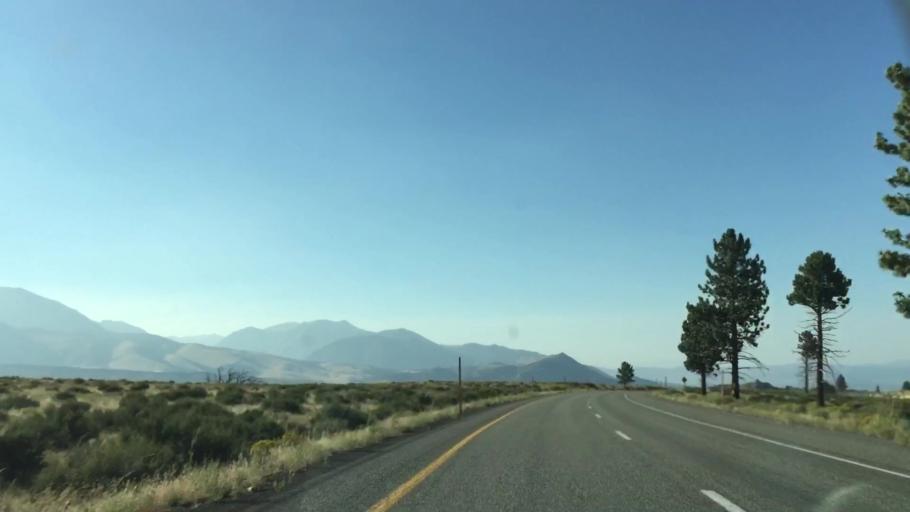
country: US
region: California
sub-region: Mono County
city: Mammoth Lakes
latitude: 37.8315
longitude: -119.0684
